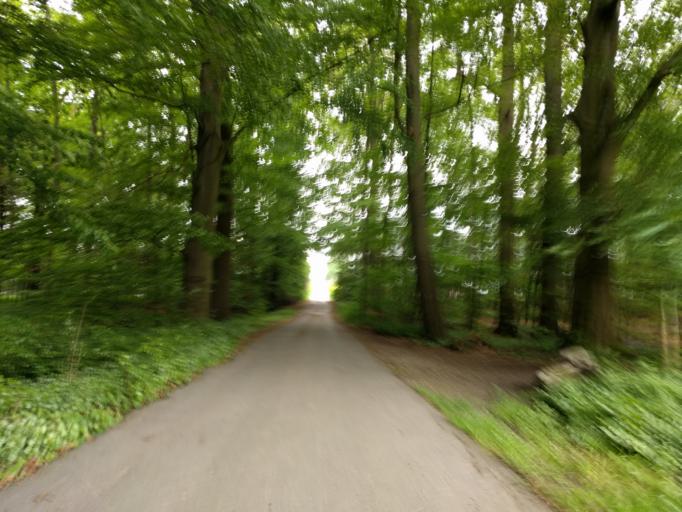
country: DE
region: North Rhine-Westphalia
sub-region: Regierungsbezirk Detmold
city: Bielefeld
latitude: 52.0441
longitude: 8.5704
